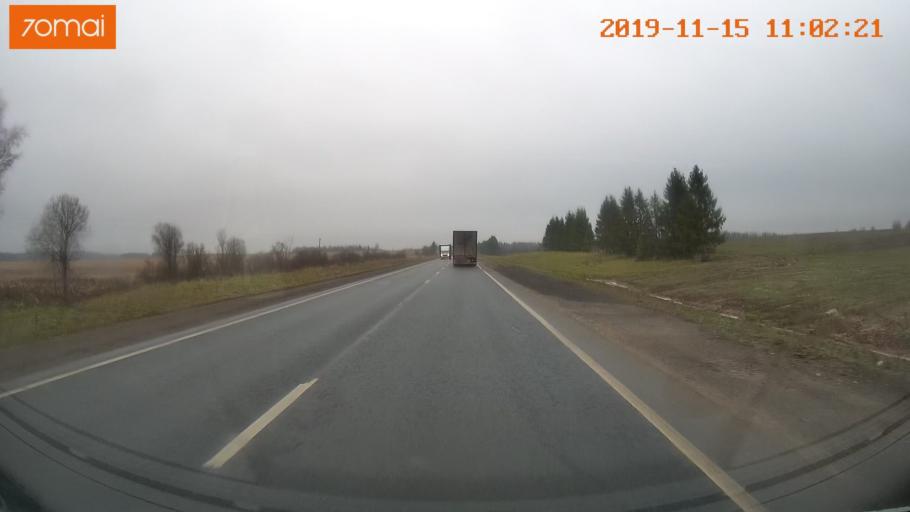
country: RU
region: Vologda
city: Chebsara
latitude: 59.1291
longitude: 38.9394
